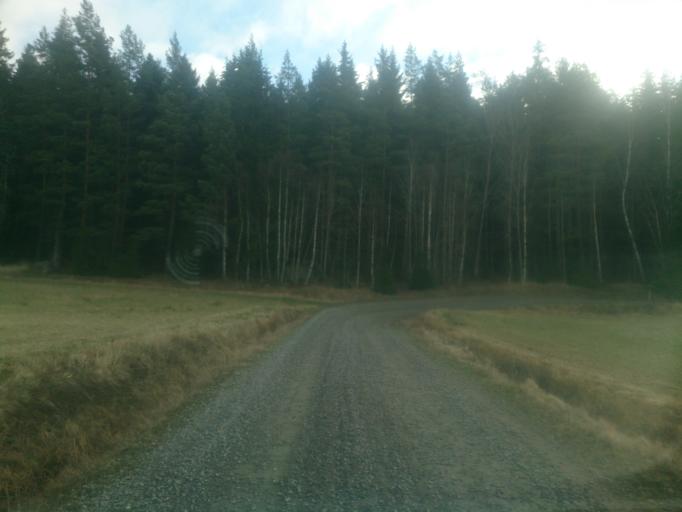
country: SE
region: OEstergoetland
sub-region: Atvidabergs Kommun
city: Atvidaberg
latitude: 58.2355
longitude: 16.1741
